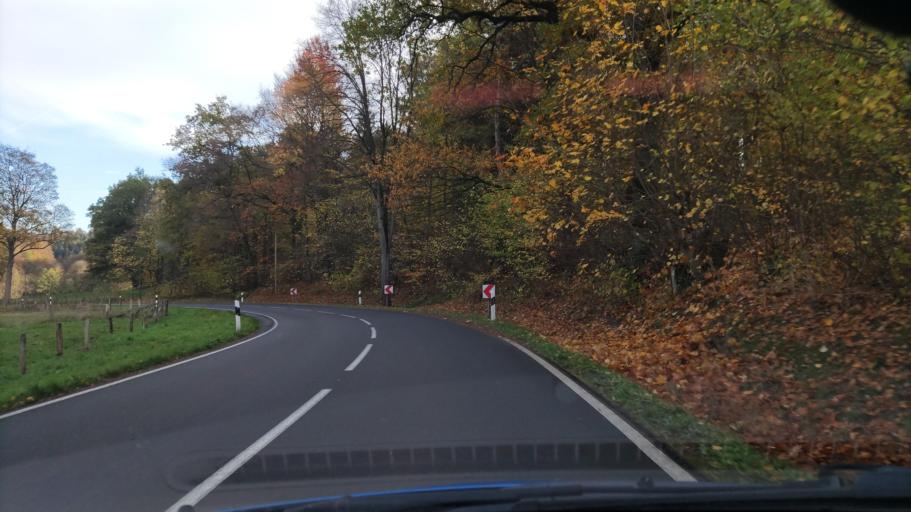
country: DE
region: Lower Saxony
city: Dassel
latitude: 51.7398
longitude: 9.7593
